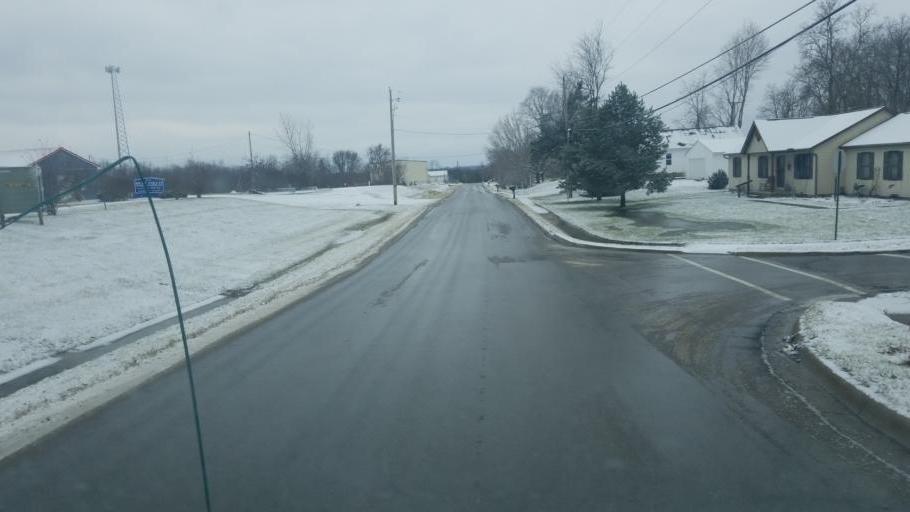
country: US
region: Ohio
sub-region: Licking County
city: Johnstown
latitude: 40.1470
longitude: -82.6863
